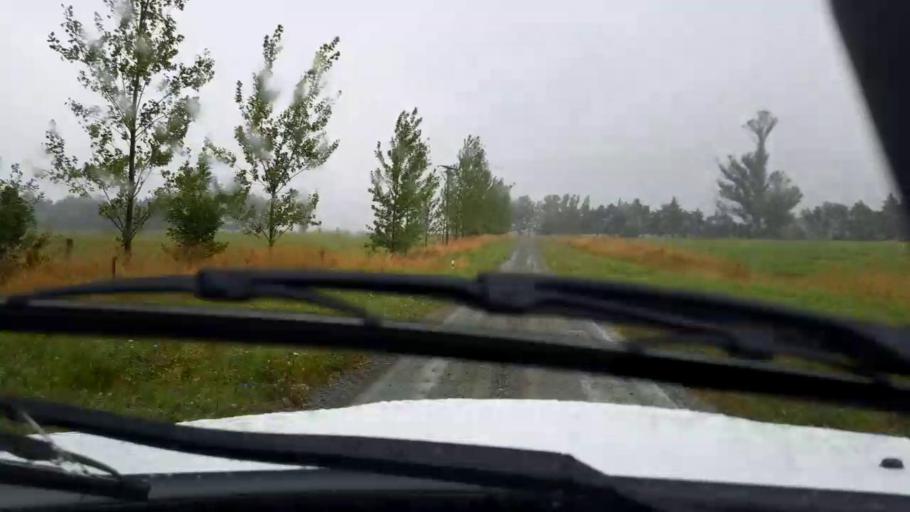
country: NZ
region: Canterbury
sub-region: Timaru District
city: Pleasant Point
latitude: -44.2007
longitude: 171.0901
